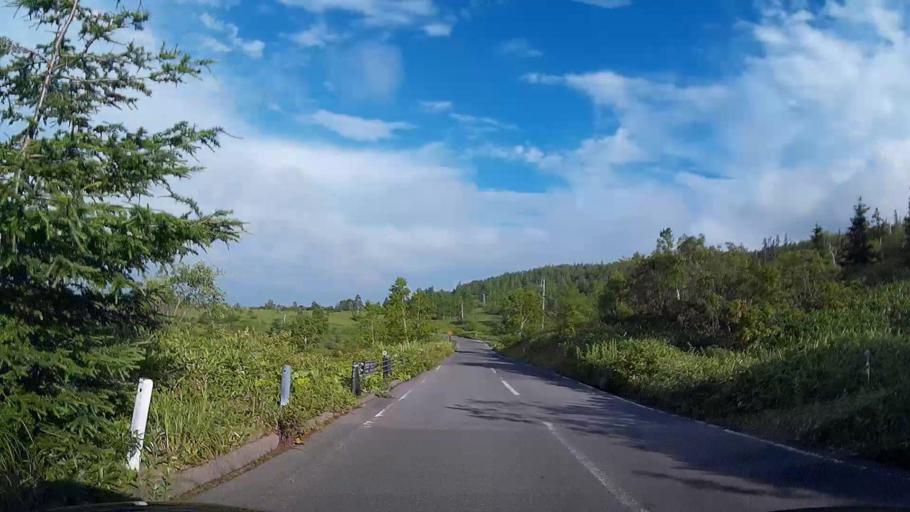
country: JP
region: Nagano
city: Nakano
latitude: 36.6358
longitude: 138.5400
